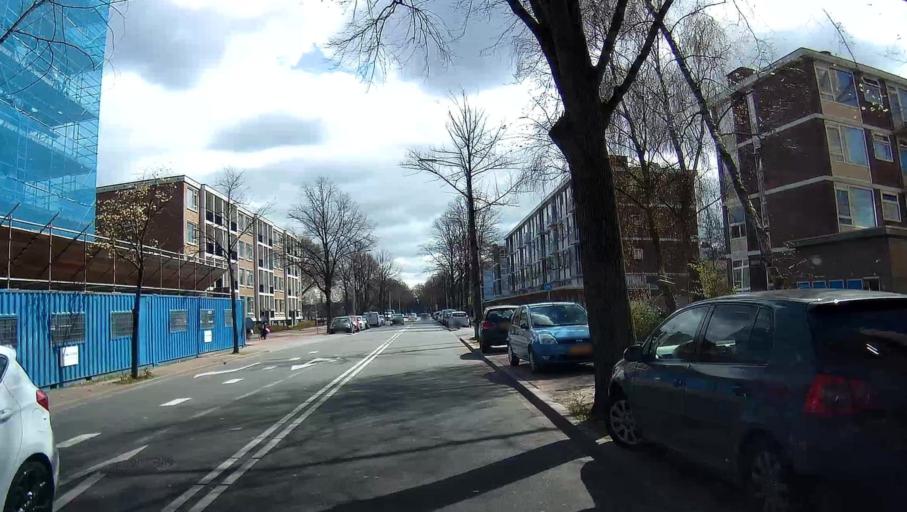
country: NL
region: South Holland
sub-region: Gemeente Westland
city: Kwintsheul
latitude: 52.0455
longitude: 4.2552
